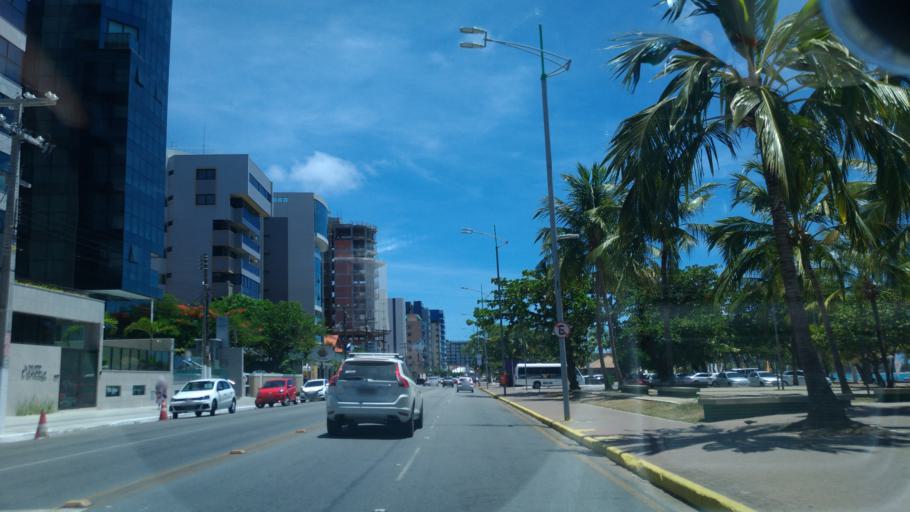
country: BR
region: Alagoas
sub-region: Maceio
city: Maceio
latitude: -9.6675
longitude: -35.7130
